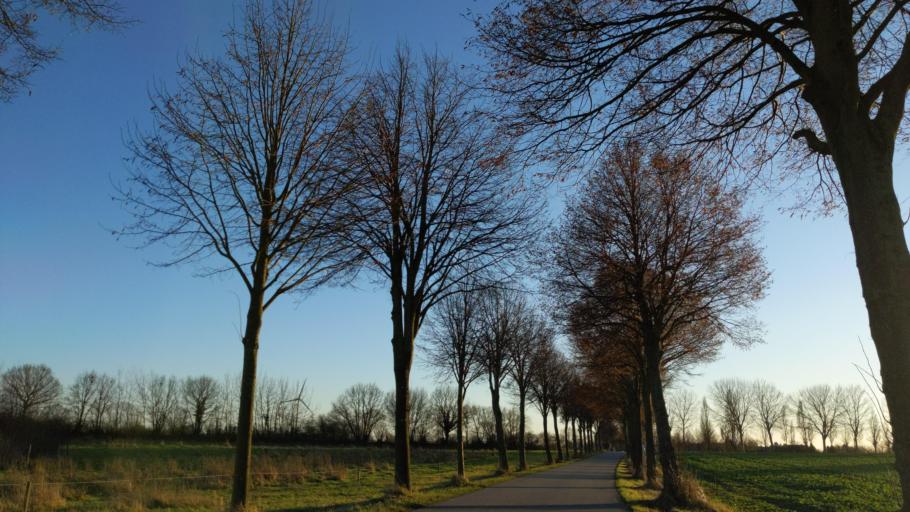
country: DE
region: Schleswig-Holstein
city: Travemuende
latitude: 53.9481
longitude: 10.8160
